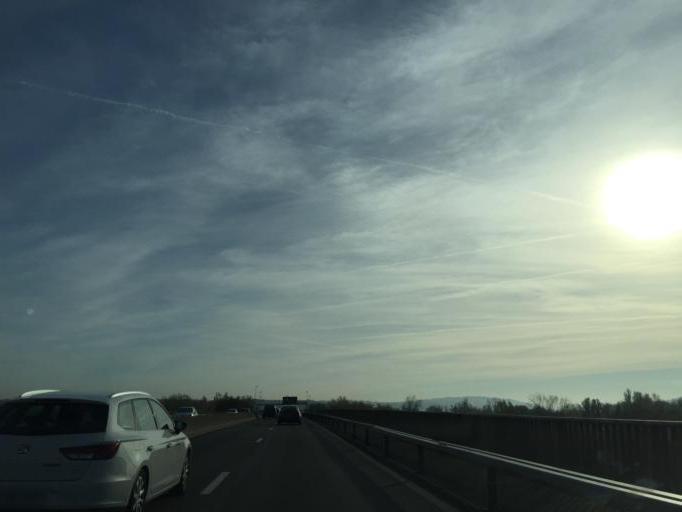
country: FR
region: Rhone-Alpes
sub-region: Departement du Rhone
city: Givors
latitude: 45.5895
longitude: 4.7767
